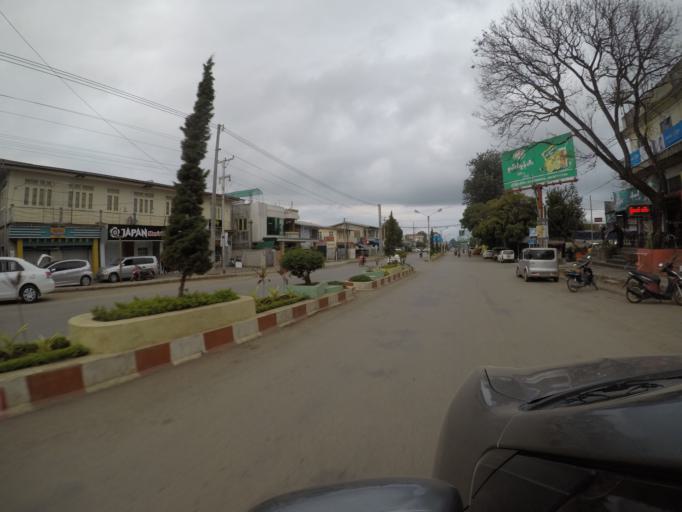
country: MM
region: Shan
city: Taunggyi
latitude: 20.7952
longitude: 97.0374
